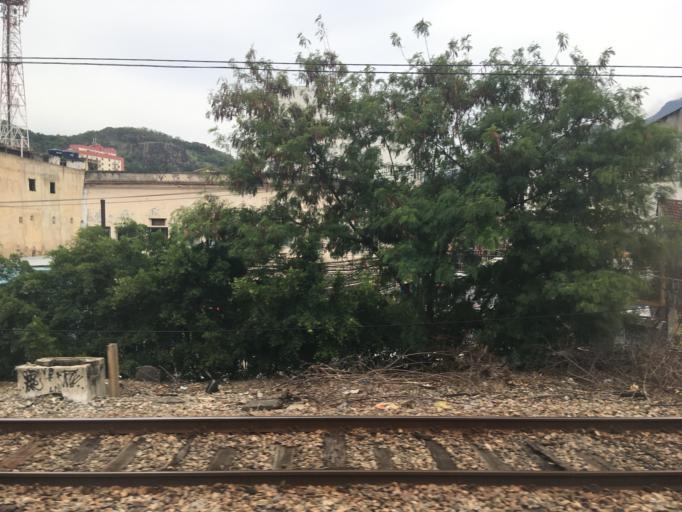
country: BR
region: Rio de Janeiro
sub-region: Rio De Janeiro
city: Rio de Janeiro
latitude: -22.9031
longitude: -43.2698
